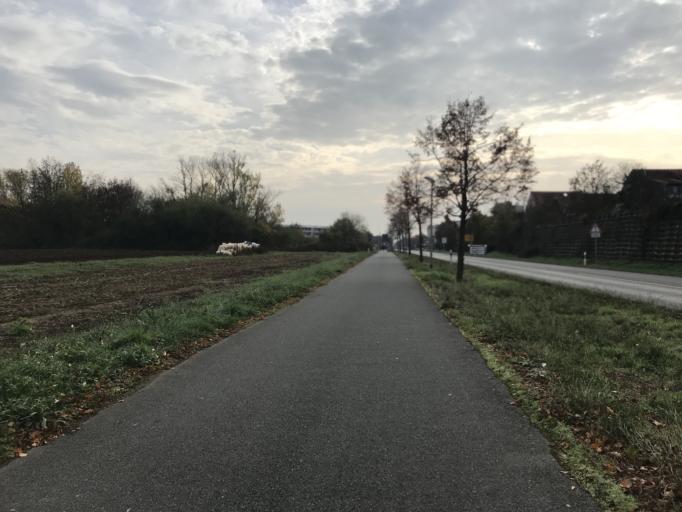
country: DE
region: Hesse
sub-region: Regierungsbezirk Darmstadt
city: Ginsheim-Gustavsburg
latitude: 49.9782
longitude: 8.3381
